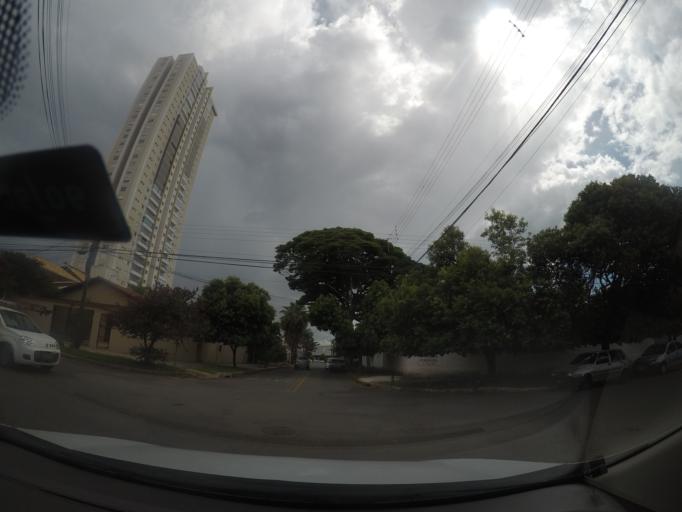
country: BR
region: Goias
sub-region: Goiania
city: Goiania
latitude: -16.7069
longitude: -49.2778
